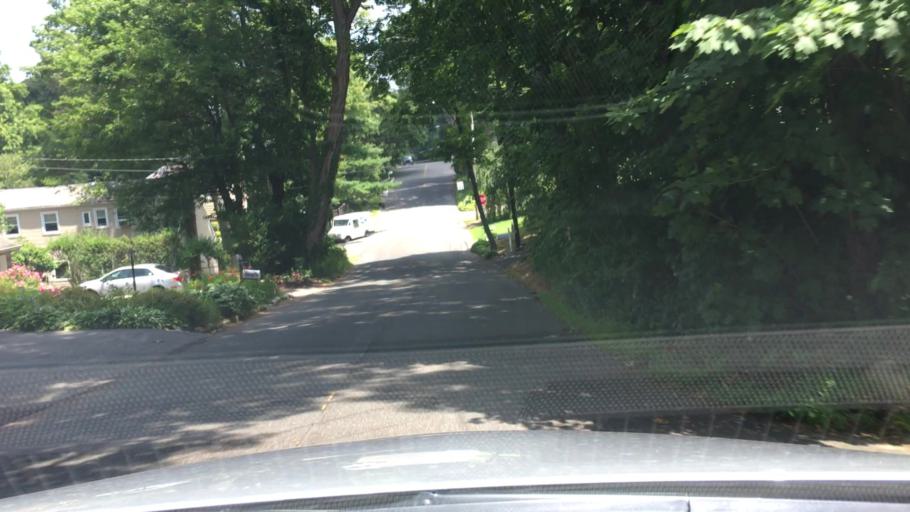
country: US
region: New York
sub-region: Suffolk County
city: West Hills
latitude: 40.8202
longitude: -73.4409
